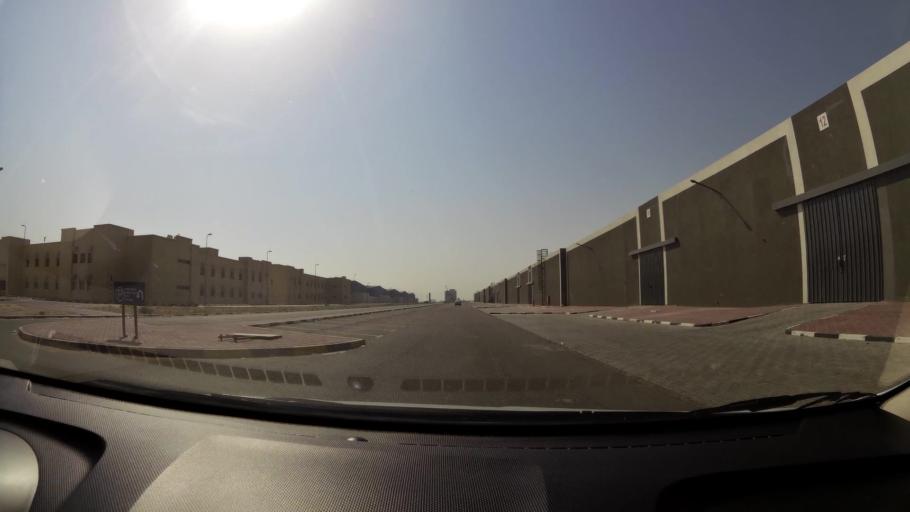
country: AE
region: Ajman
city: Ajman
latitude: 25.4255
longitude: 55.5275
